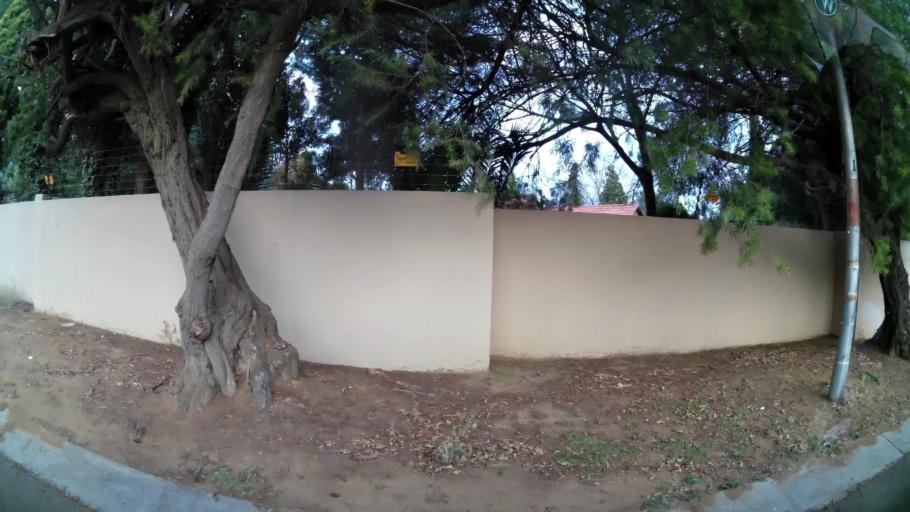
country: ZA
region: Gauteng
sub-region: Ekurhuleni Metropolitan Municipality
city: Benoni
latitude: -26.1720
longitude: 28.3069
